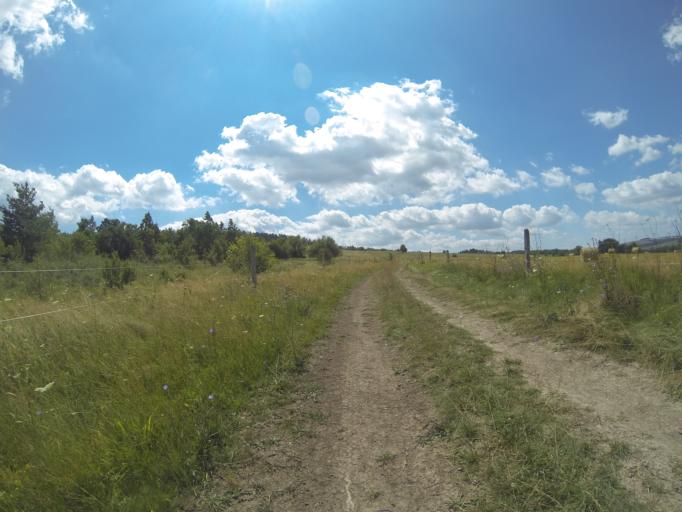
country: RO
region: Brasov
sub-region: Comuna Sercaia
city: Sercaia
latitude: 45.8700
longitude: 25.0970
